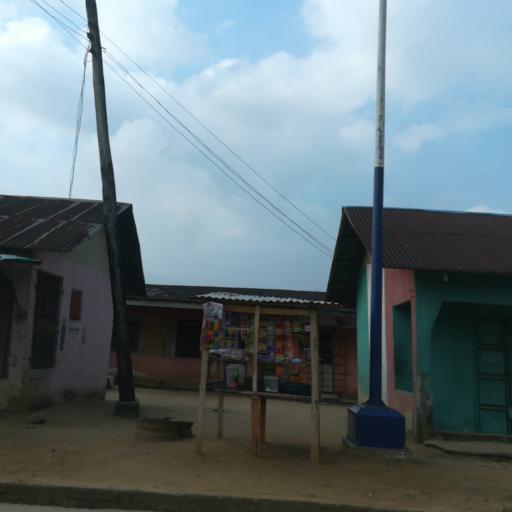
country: NG
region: Rivers
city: Okrika
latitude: 4.7808
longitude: 7.1532
